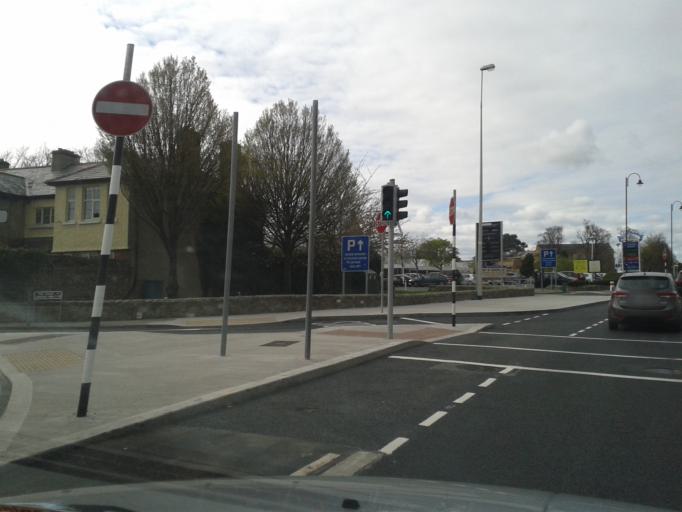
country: IE
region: Leinster
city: Blackrock
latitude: 53.3007
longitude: -6.1800
